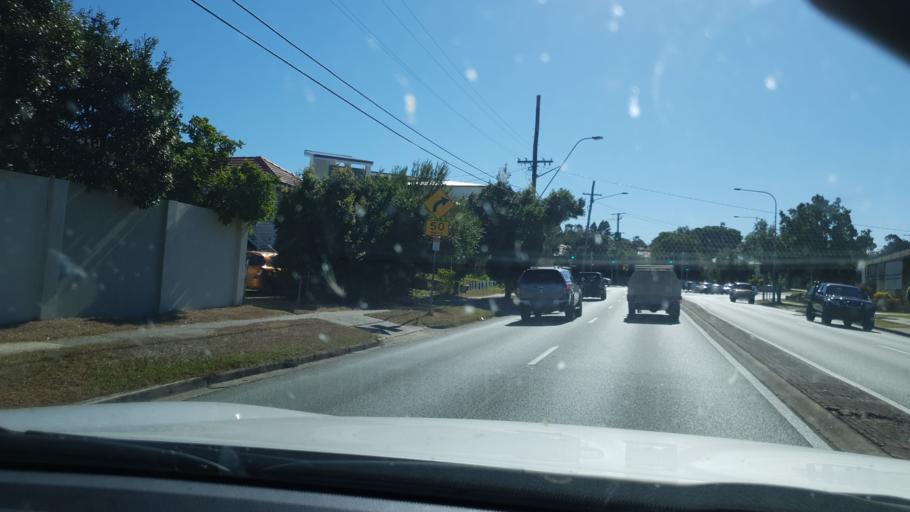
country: AU
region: Queensland
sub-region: Brisbane
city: Everton Park
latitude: -27.4034
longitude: 152.9877
